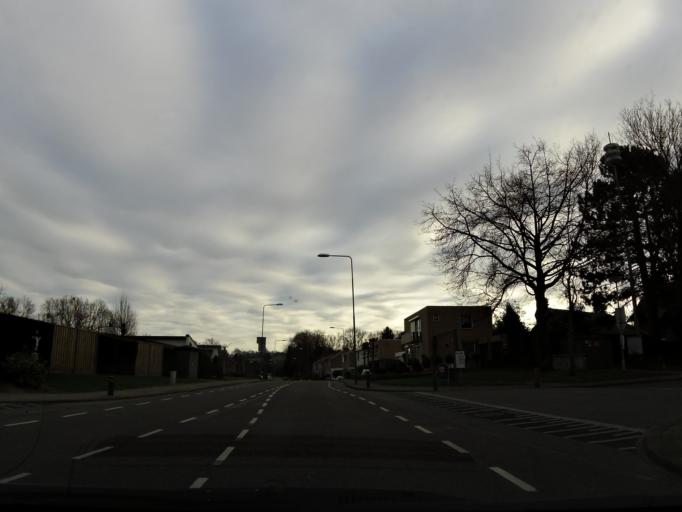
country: NL
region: Limburg
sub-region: Gemeente Schinnen
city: Puth
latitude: 50.9409
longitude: 5.8428
